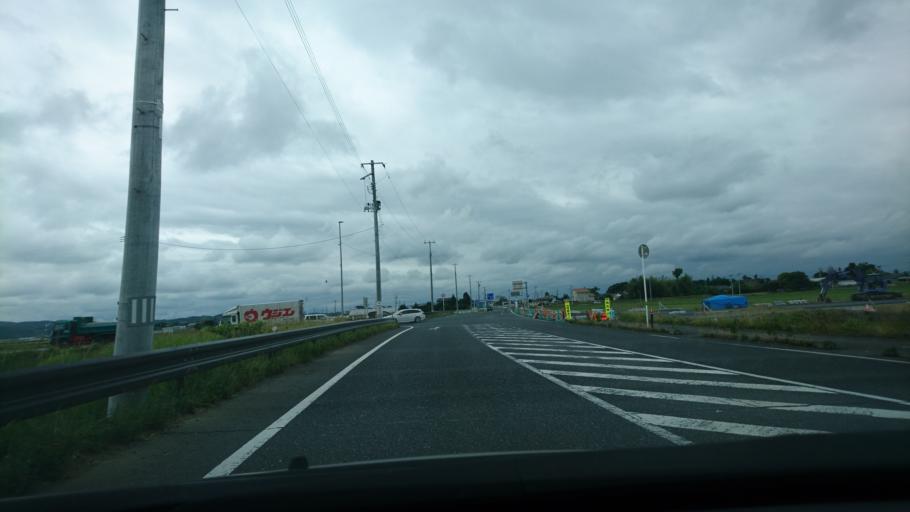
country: JP
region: Miyagi
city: Wakuya
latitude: 38.6782
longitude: 141.2606
